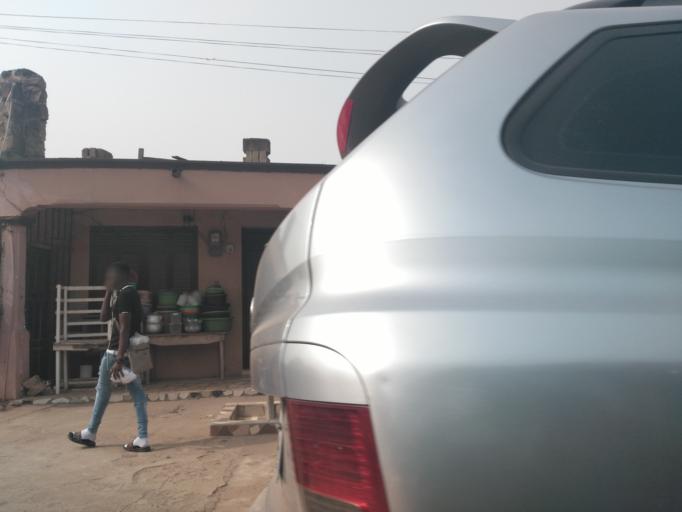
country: GH
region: Ashanti
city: Kumasi
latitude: 6.6815
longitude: -1.6093
